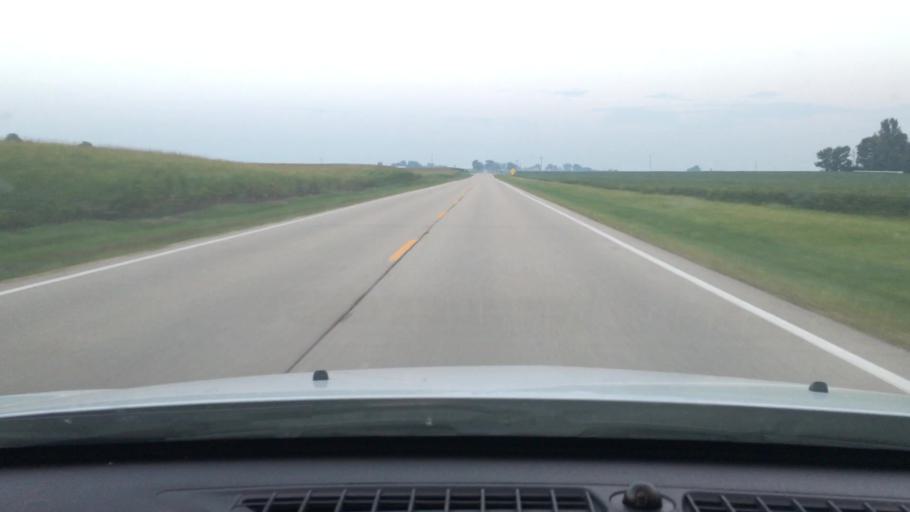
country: US
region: Illinois
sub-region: Ogle County
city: Rochelle
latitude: 41.8511
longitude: -89.0733
